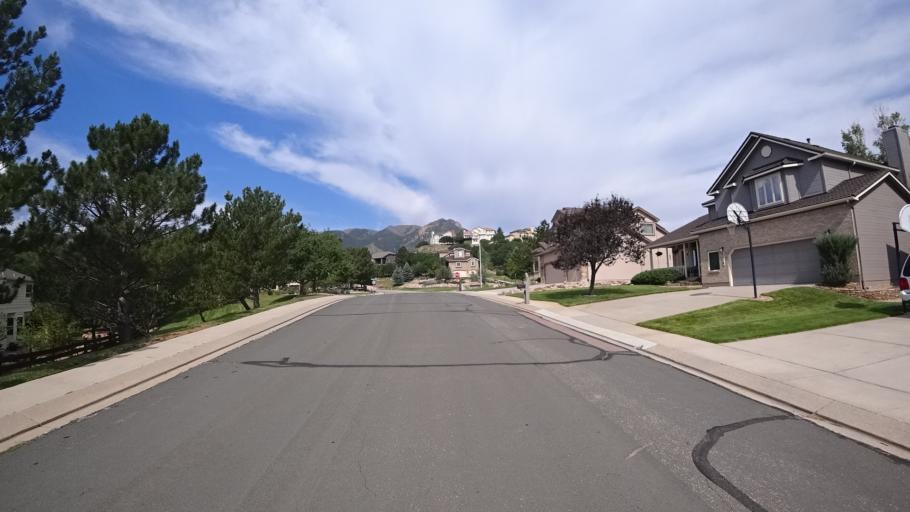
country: US
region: Colorado
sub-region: El Paso County
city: Air Force Academy
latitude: 38.9529
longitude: -104.8624
